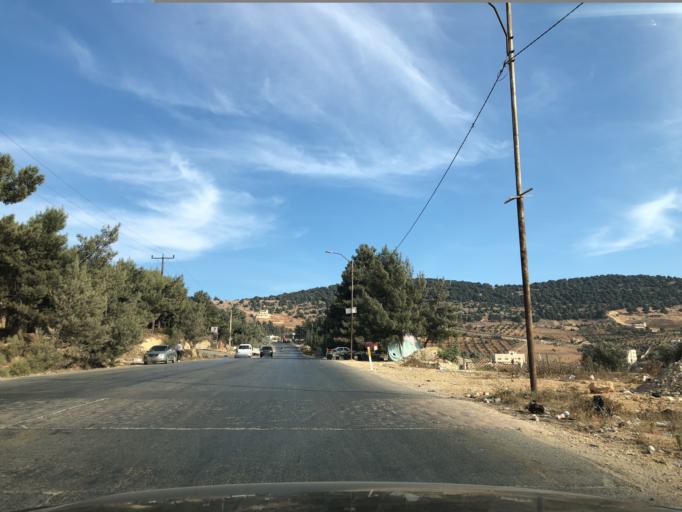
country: JO
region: Irbid
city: `Anjarah
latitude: 32.3146
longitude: 35.7721
